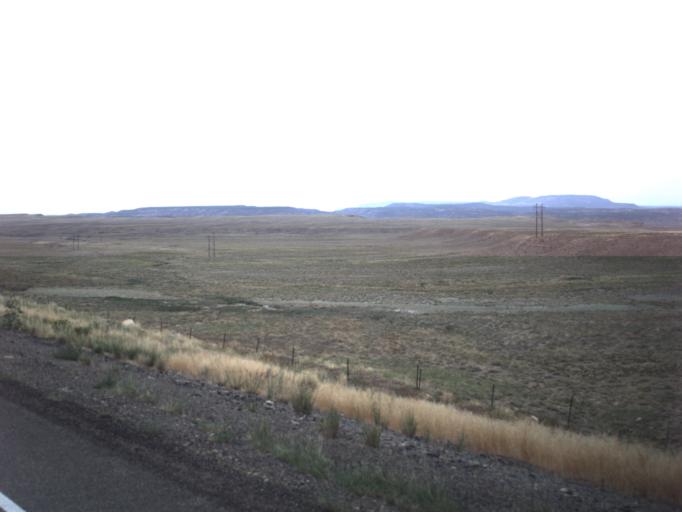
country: US
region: Utah
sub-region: Carbon County
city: East Carbon City
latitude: 39.4894
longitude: -110.5176
